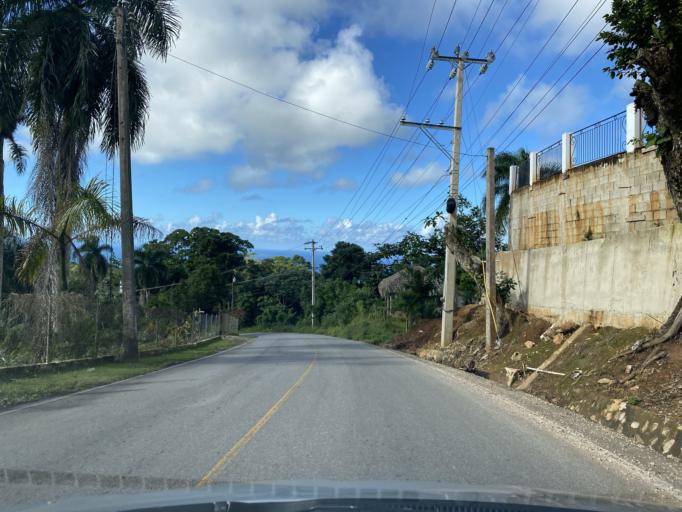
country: DO
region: Samana
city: Las Terrenas
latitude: 19.2750
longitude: -69.5501
